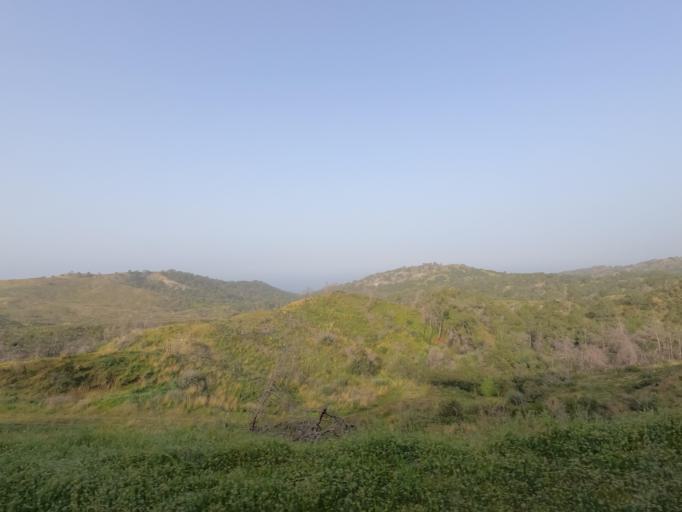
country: CY
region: Pafos
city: Polis
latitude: 35.0006
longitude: 32.3361
